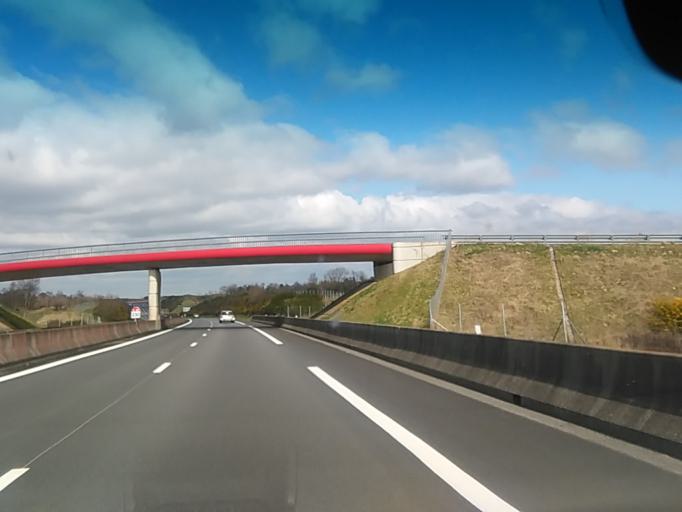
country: FR
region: Lower Normandy
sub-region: Departement du Calvados
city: Orbec
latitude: 49.0143
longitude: 0.4462
